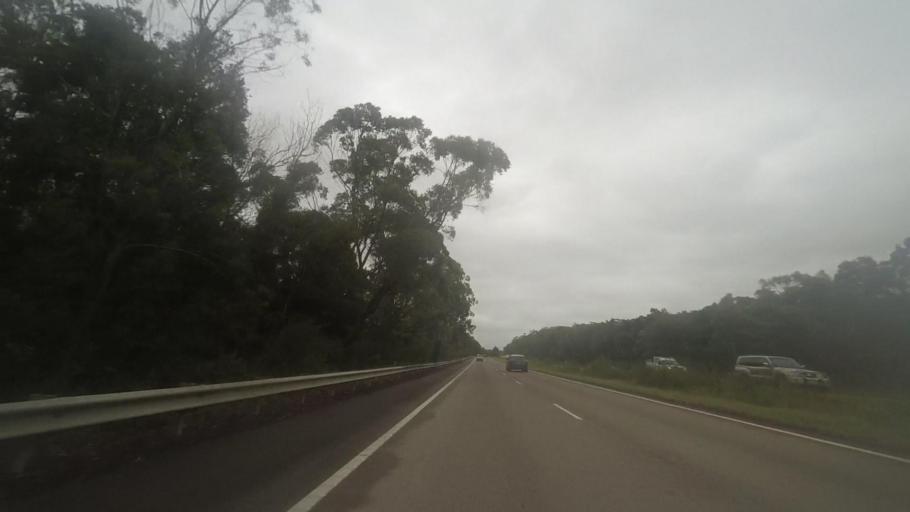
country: AU
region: New South Wales
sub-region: Port Stephens Shire
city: Medowie
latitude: -32.6754
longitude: 151.8251
